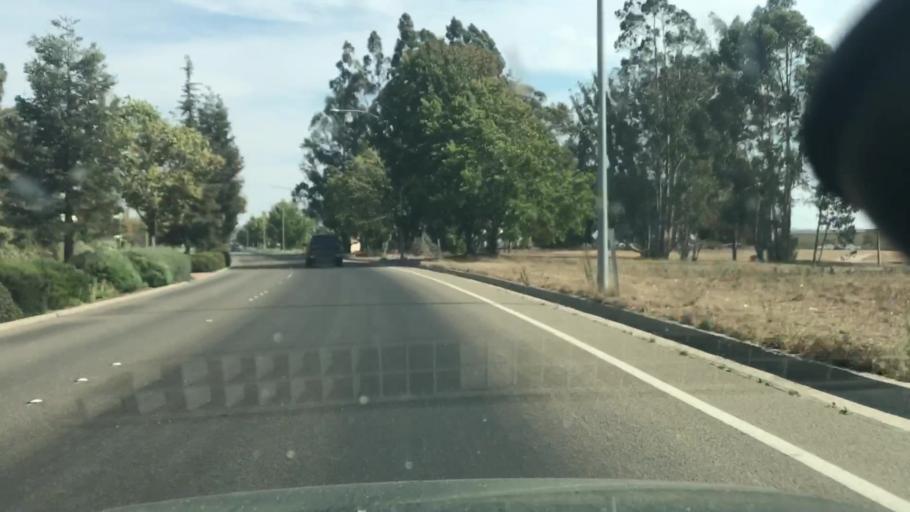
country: US
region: California
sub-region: Santa Barbara County
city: Orcutt
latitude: 34.9066
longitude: -120.4537
